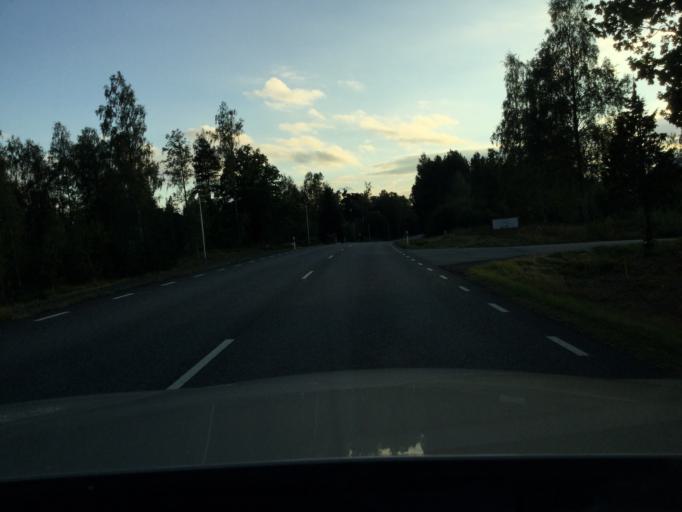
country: SE
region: Kronoberg
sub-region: Almhults Kommun
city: AElmhult
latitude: 56.6512
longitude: 14.2401
